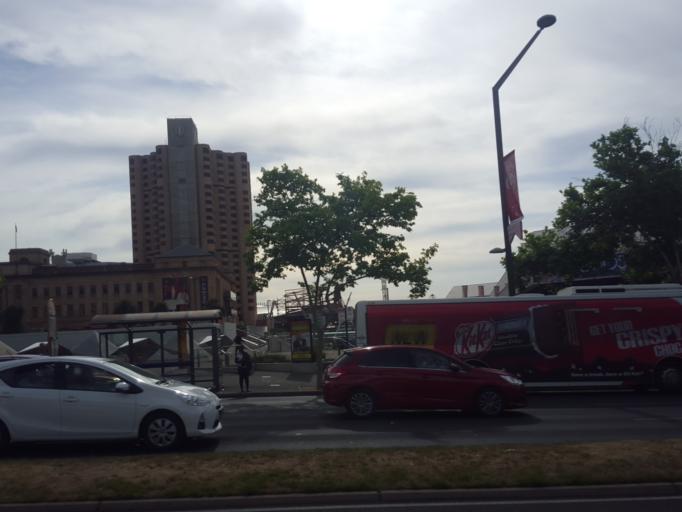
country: AU
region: South Australia
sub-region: Adelaide
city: Adelaide
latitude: -34.9201
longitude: 138.5993
